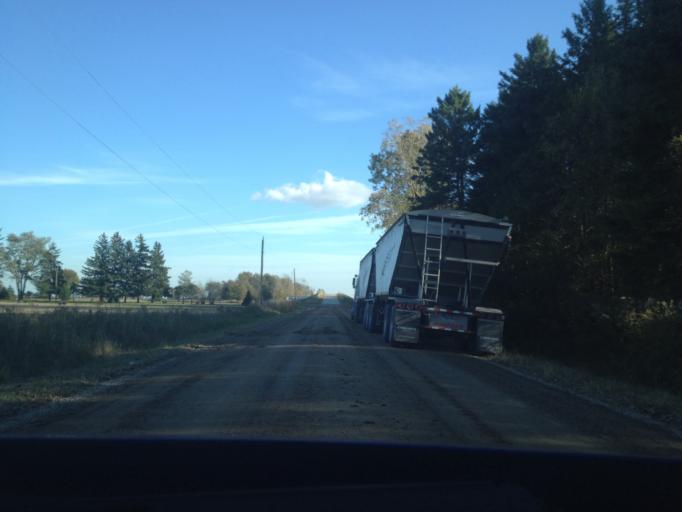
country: CA
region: Ontario
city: Delaware
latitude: 42.6560
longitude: -81.5531
